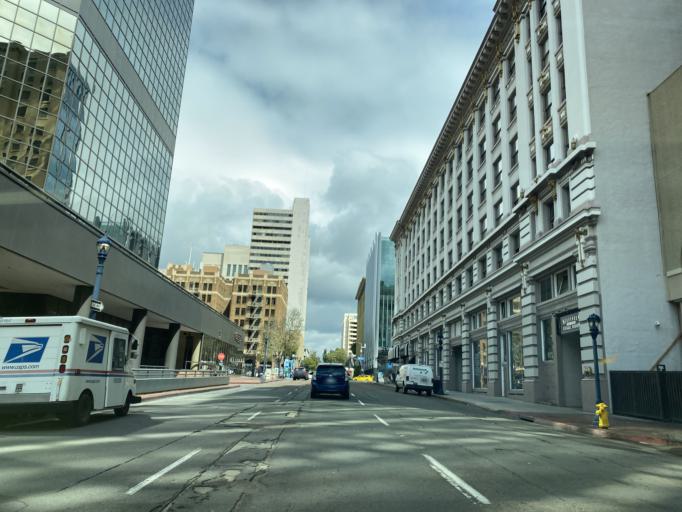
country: US
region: California
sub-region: San Diego County
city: San Diego
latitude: 32.7146
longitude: -117.1638
